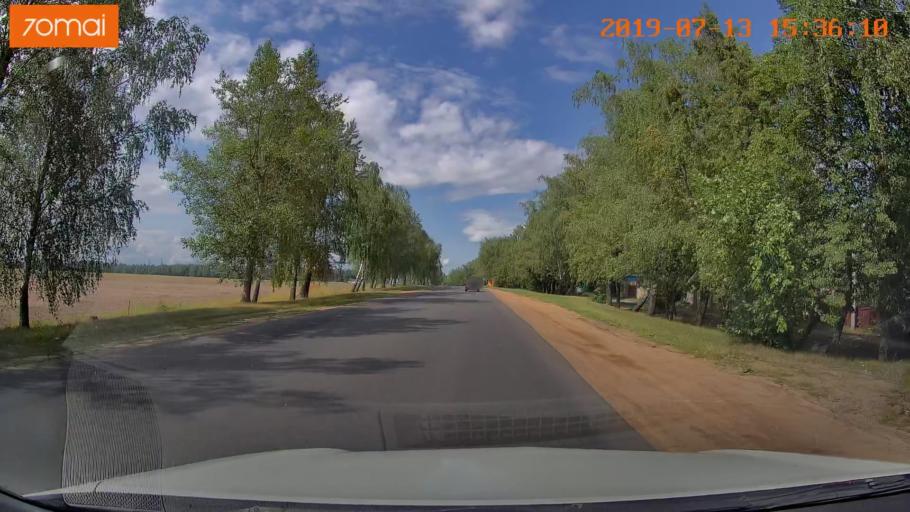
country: BY
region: Mogilev
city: Babruysk
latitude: 53.1290
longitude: 29.1668
